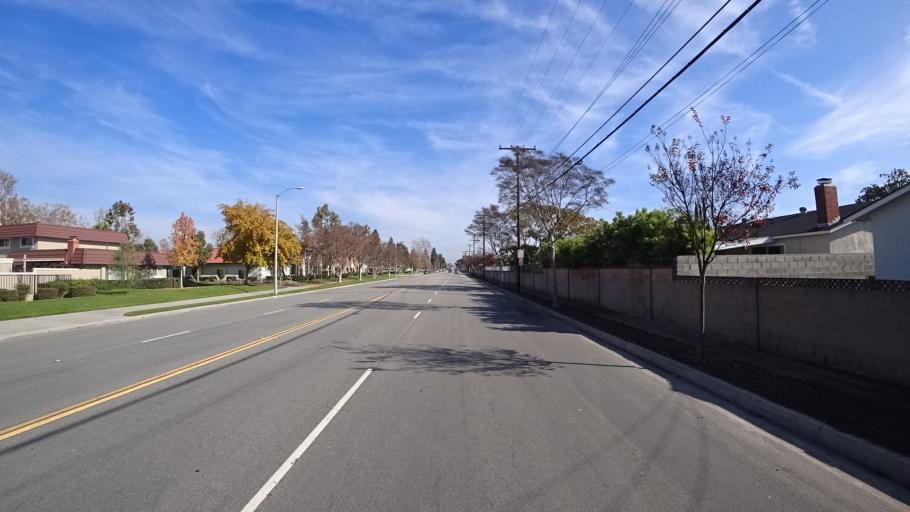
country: US
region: California
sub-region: Orange County
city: Stanton
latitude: 33.7956
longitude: -118.0171
